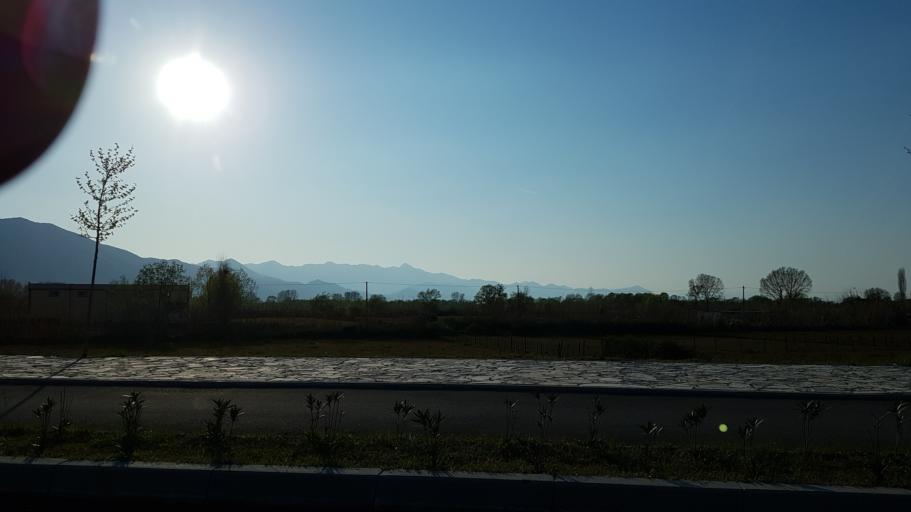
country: AL
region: Shkoder
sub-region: Rrethi i Shkodres
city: Shkoder
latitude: 42.0738
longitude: 19.4898
